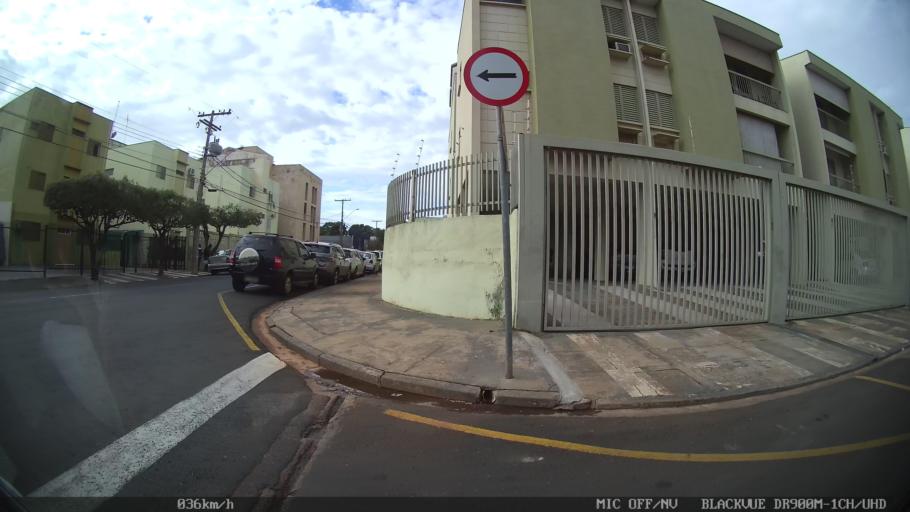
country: BR
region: Sao Paulo
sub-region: Sao Jose Do Rio Preto
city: Sao Jose do Rio Preto
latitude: -20.8297
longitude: -49.3991
